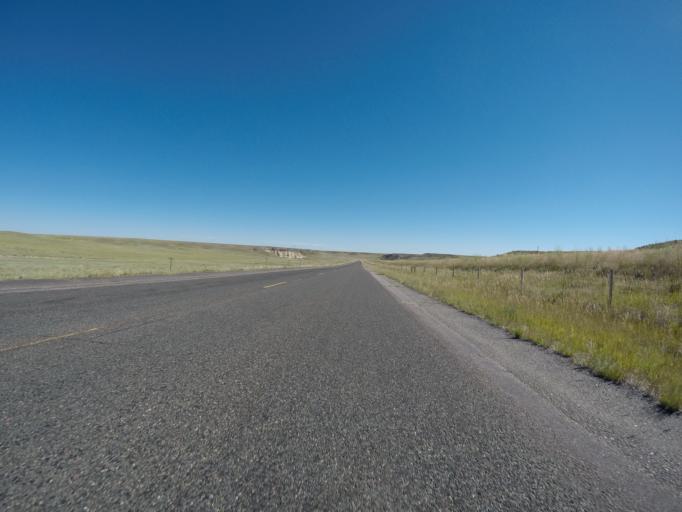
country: US
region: Wyoming
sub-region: Platte County
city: Wheatland
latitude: 41.6861
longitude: -104.8320
